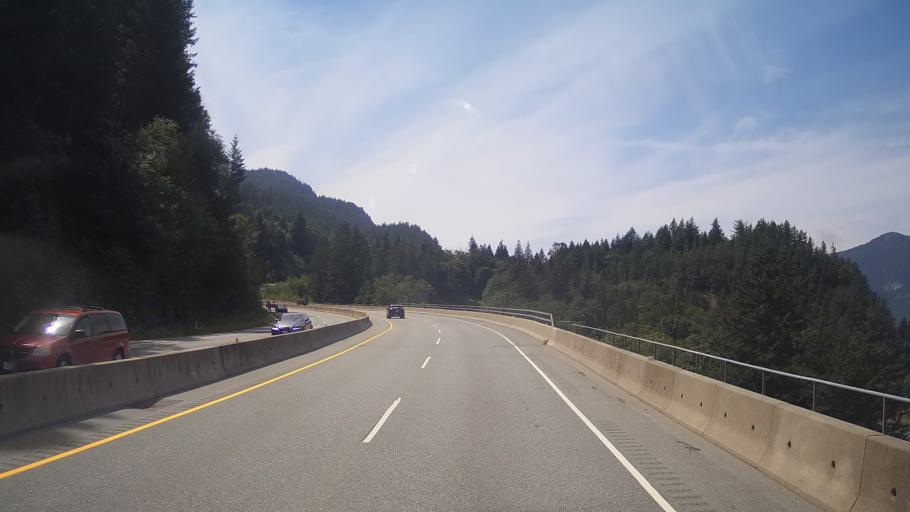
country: CA
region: British Columbia
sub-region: Greater Vancouver Regional District
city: Lions Bay
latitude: 49.5507
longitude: -123.2360
